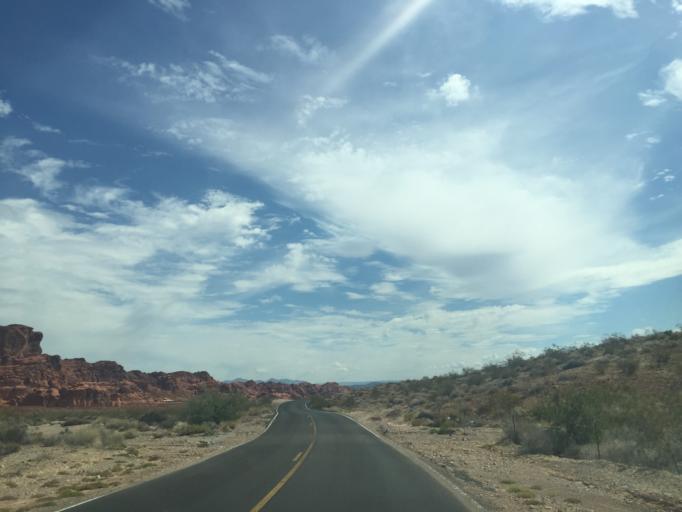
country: US
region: Nevada
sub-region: Clark County
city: Moapa Valley
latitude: 36.4251
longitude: -114.5307
